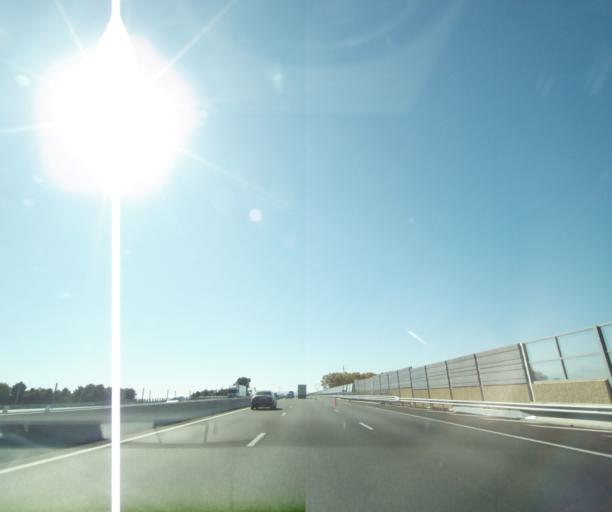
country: FR
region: Languedoc-Roussillon
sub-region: Departement de l'Herault
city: Lattes
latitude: 43.5916
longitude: 3.9134
